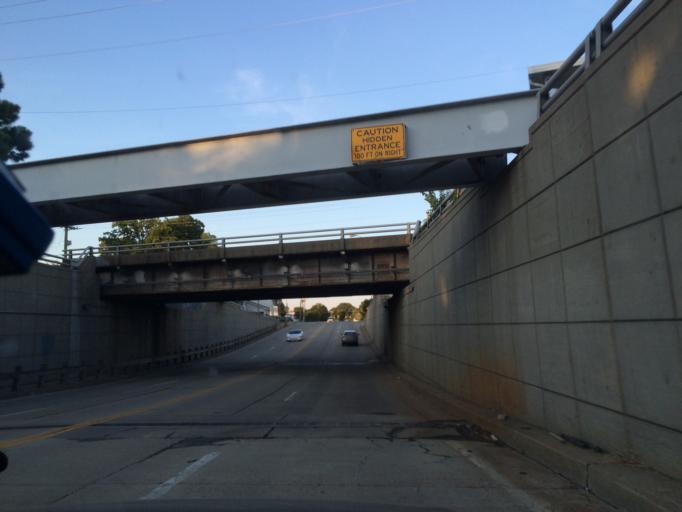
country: US
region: Virginia
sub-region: City of Newport News
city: Newport News
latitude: 37.0340
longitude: -76.4592
